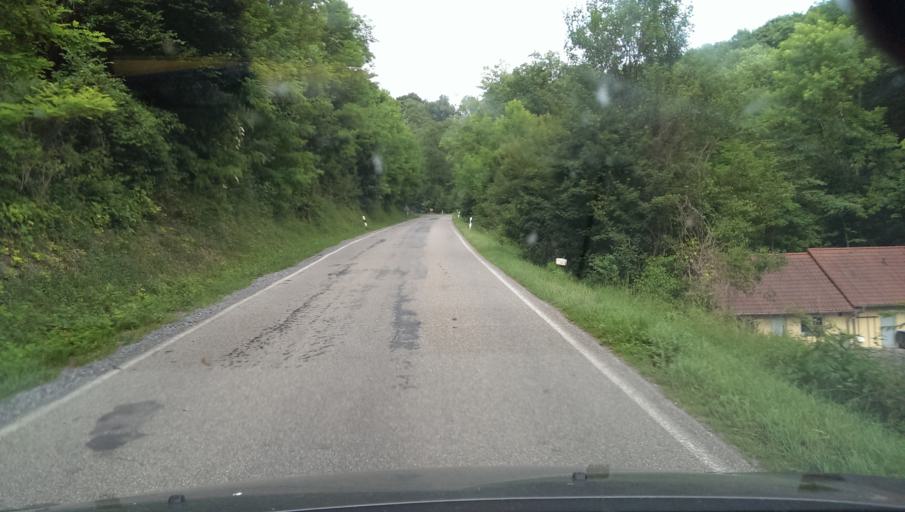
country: DE
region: Baden-Wuerttemberg
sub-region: Regierungsbezirk Stuttgart
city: Zweiflingen
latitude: 49.2576
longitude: 9.5341
